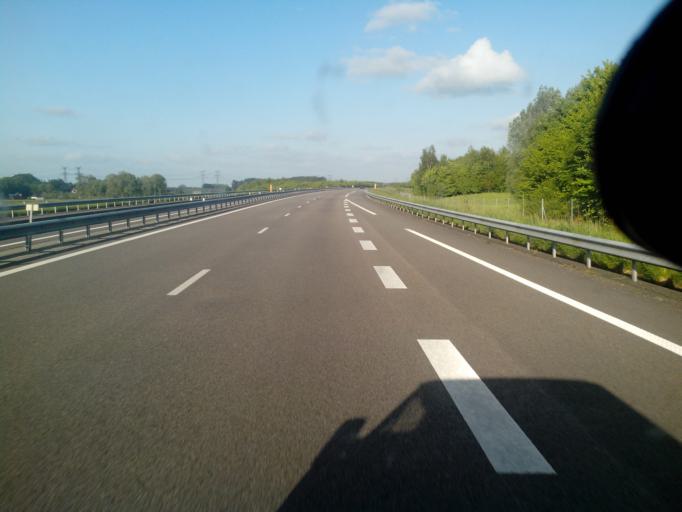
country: FR
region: Haute-Normandie
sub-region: Departement de la Seine-Maritime
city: Totes
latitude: 49.6389
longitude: 1.0587
